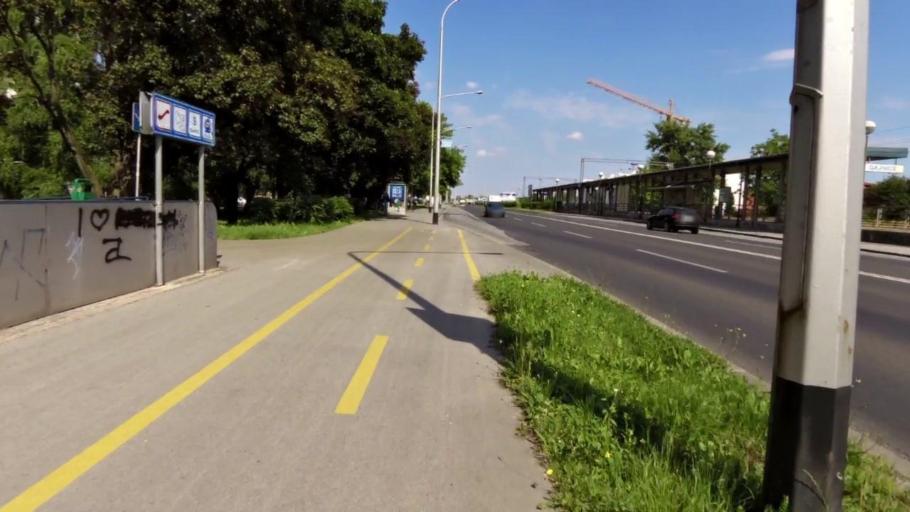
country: HR
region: Grad Zagreb
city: Stenjevec
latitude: 45.8138
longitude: 15.8729
